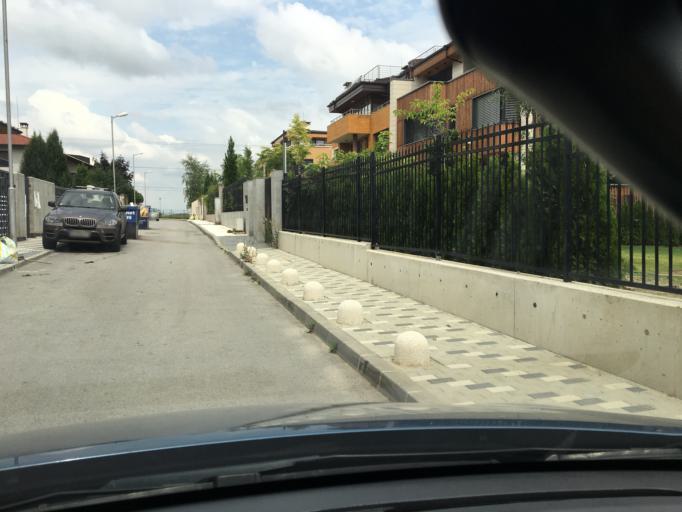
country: BG
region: Sofia-Capital
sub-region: Stolichna Obshtina
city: Sofia
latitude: 42.6160
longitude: 23.3668
